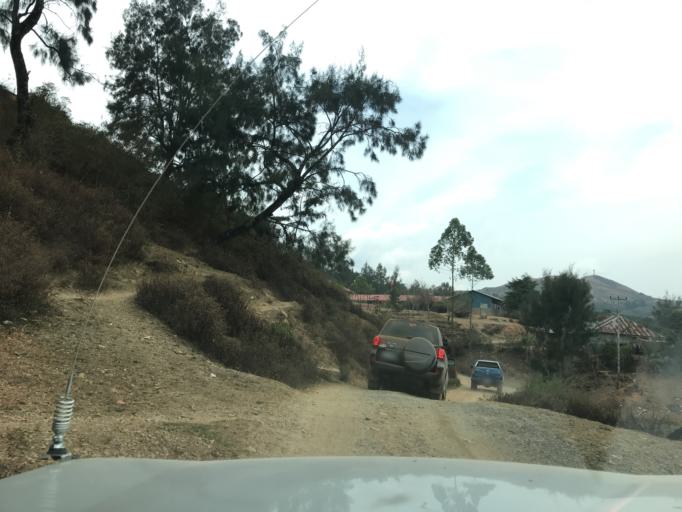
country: TL
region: Ermera
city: Gleno
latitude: -8.8282
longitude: 125.4538
